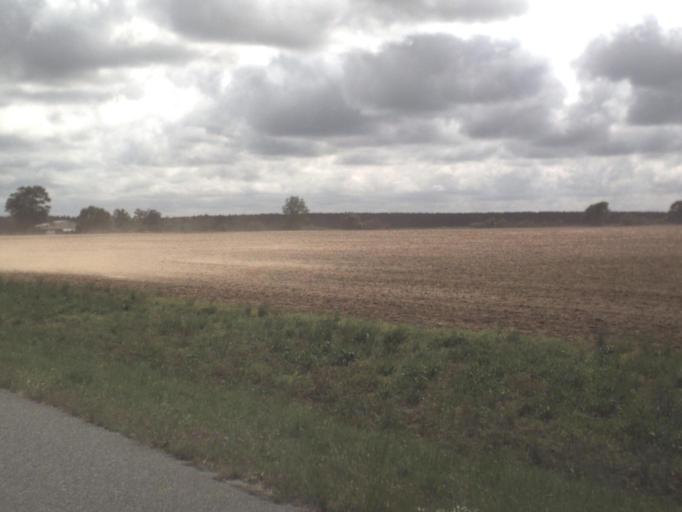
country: US
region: Florida
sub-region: Santa Rosa County
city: Point Baker
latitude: 30.7737
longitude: -87.0928
